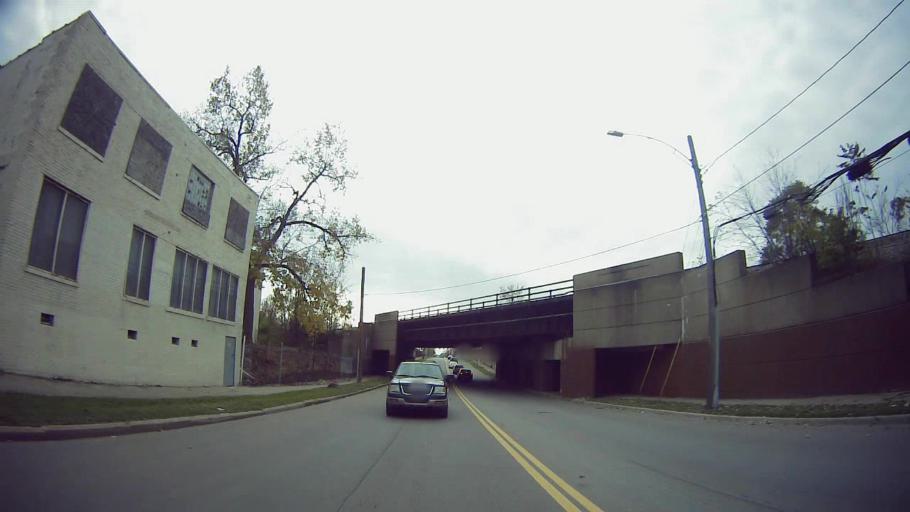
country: US
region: Michigan
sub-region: Wayne County
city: Highland Park
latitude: 42.4338
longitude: -83.1024
